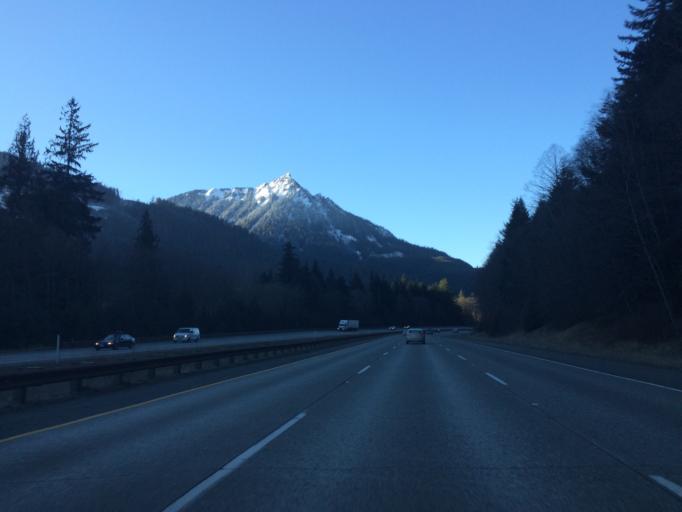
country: US
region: Washington
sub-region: King County
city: Tanner
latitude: 47.4049
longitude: -121.5666
